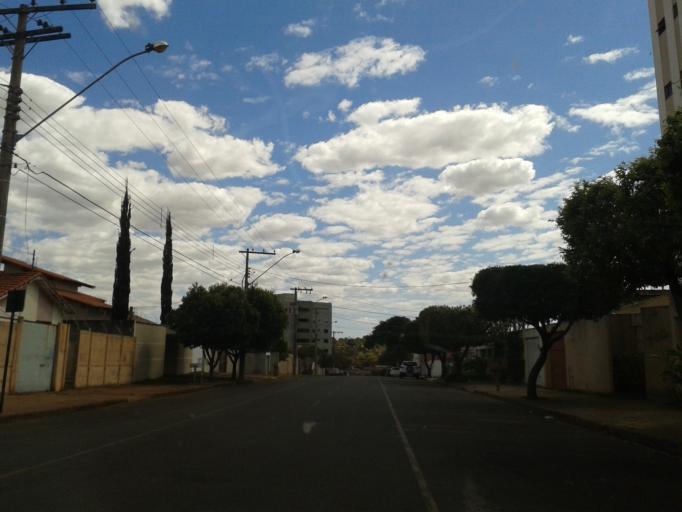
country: BR
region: Minas Gerais
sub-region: Ituiutaba
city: Ituiutaba
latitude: -18.9633
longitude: -49.4667
